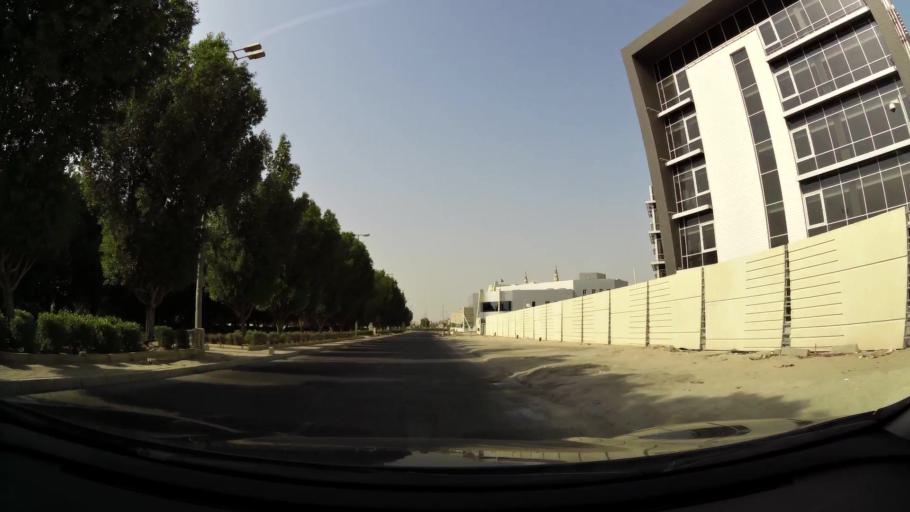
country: KW
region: Mubarak al Kabir
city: Sabah as Salim
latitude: 29.2692
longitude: 48.0517
